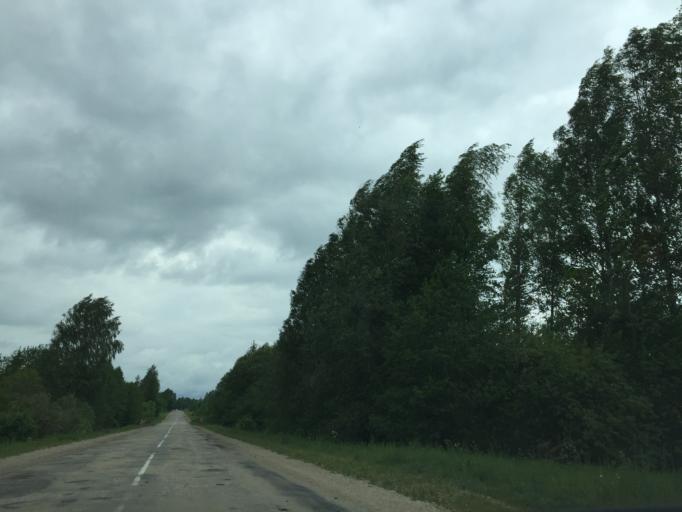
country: LV
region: Varkava
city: Vecvarkava
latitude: 56.0911
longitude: 26.5695
